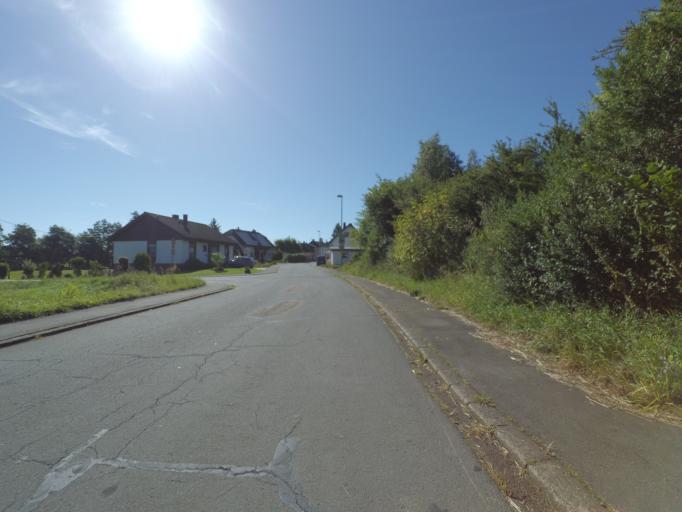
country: DE
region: Rheinland-Pfalz
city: Gillenfeld
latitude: 50.1246
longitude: 6.9014
